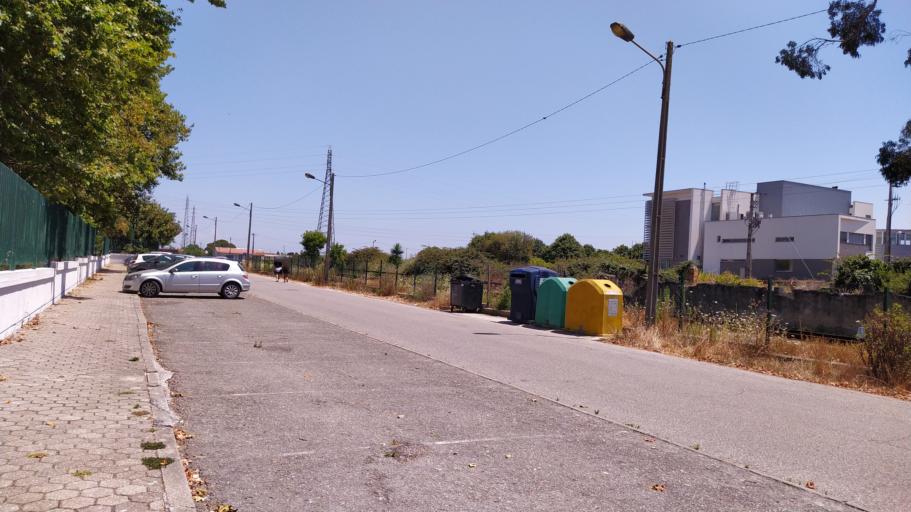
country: PT
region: Aveiro
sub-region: Aveiro
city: Aveiro
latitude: 40.6444
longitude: -8.6335
